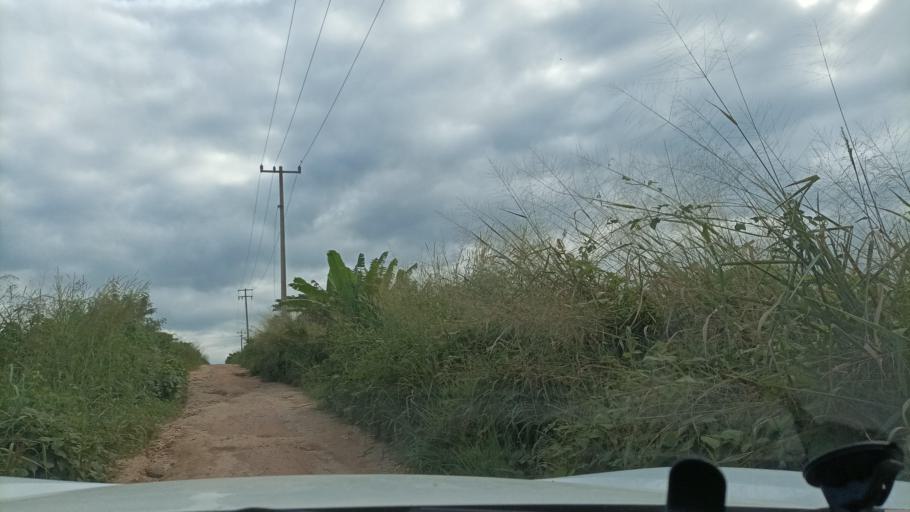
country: MX
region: Veracruz
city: Oluta
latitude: 17.9331
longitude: -94.8837
